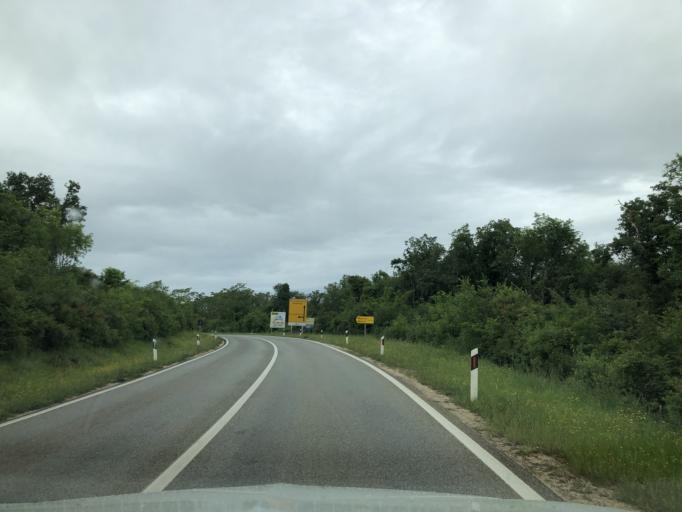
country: SI
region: Piran-Pirano
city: Seca
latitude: 45.4522
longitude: 13.6259
